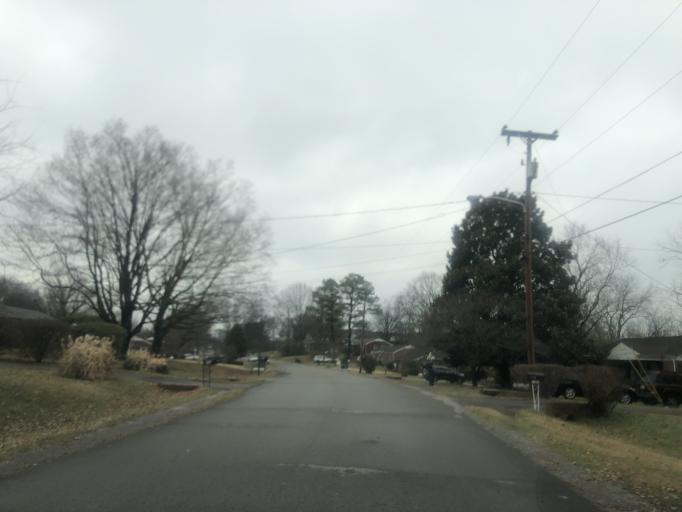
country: US
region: Tennessee
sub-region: Davidson County
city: Lakewood
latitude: 36.1526
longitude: -86.6705
